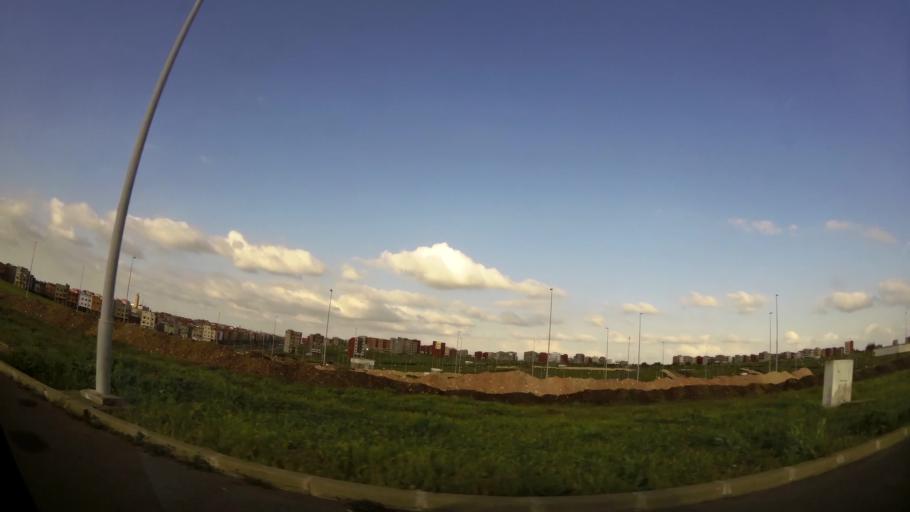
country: MA
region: Chaouia-Ouardigha
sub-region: Settat Province
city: Settat
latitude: 32.9906
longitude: -7.6447
